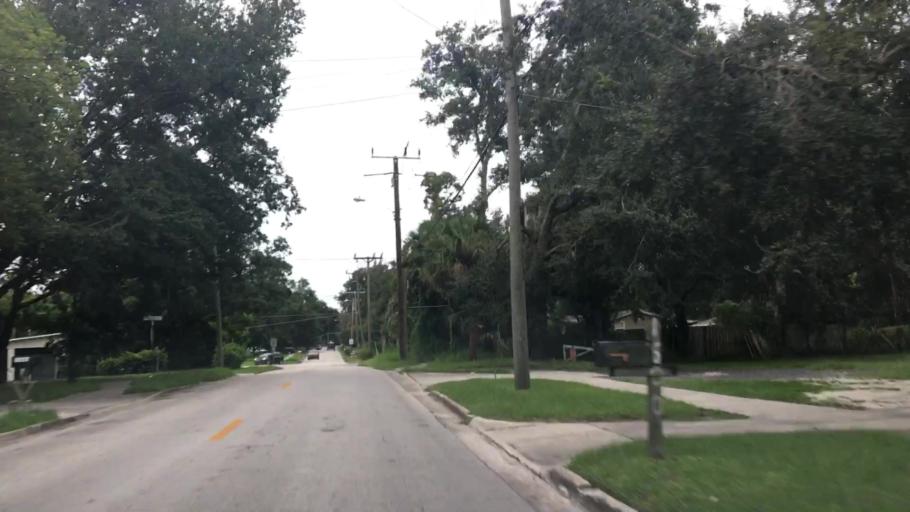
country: US
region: Florida
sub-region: Seminole County
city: Sanford
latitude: 28.7979
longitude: -81.2560
